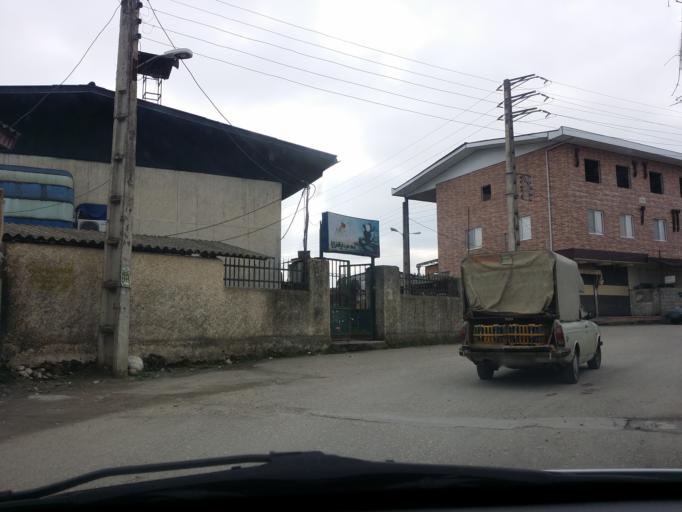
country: IR
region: Mazandaran
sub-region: Nowshahr
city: Nowshahr
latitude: 36.6485
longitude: 51.4775
